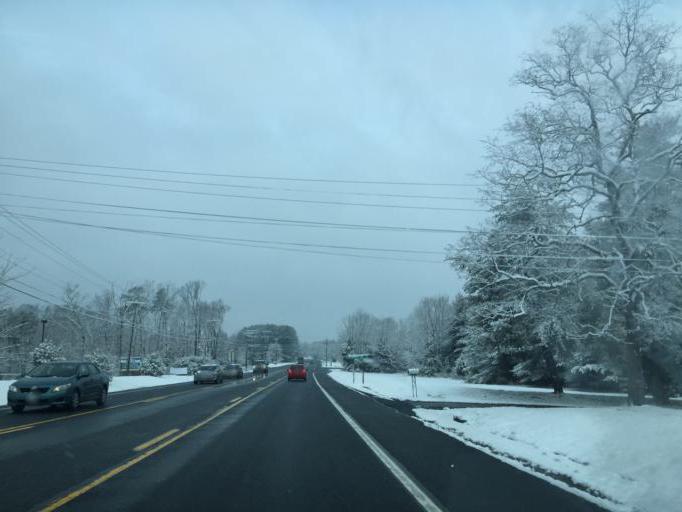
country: US
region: Maryland
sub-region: Harford County
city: Joppatowne
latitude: 39.4696
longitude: -76.3735
